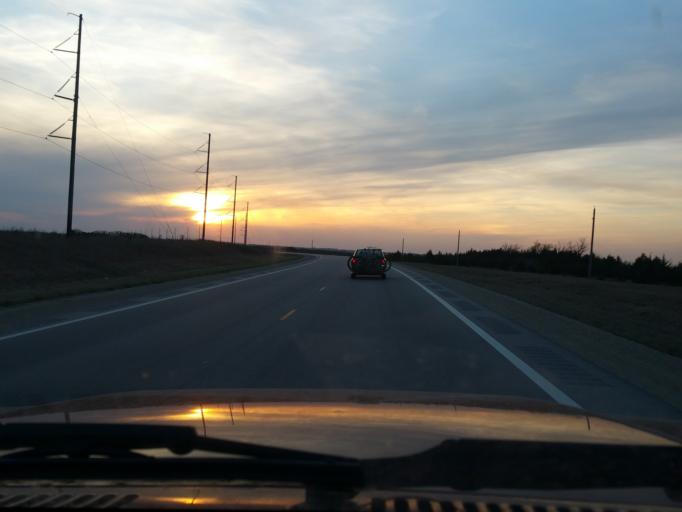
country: US
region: Kansas
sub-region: Riley County
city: Manhattan
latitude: 39.2750
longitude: -96.6973
